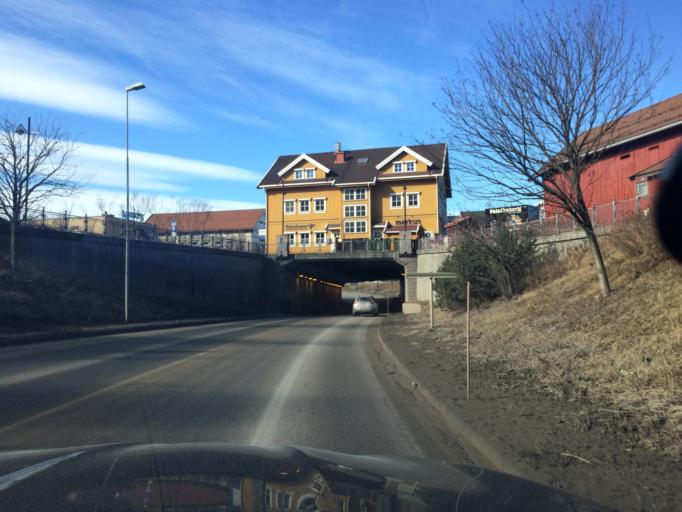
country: NO
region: Hedmark
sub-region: Elverum
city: Elverum
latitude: 60.8840
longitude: 11.5628
